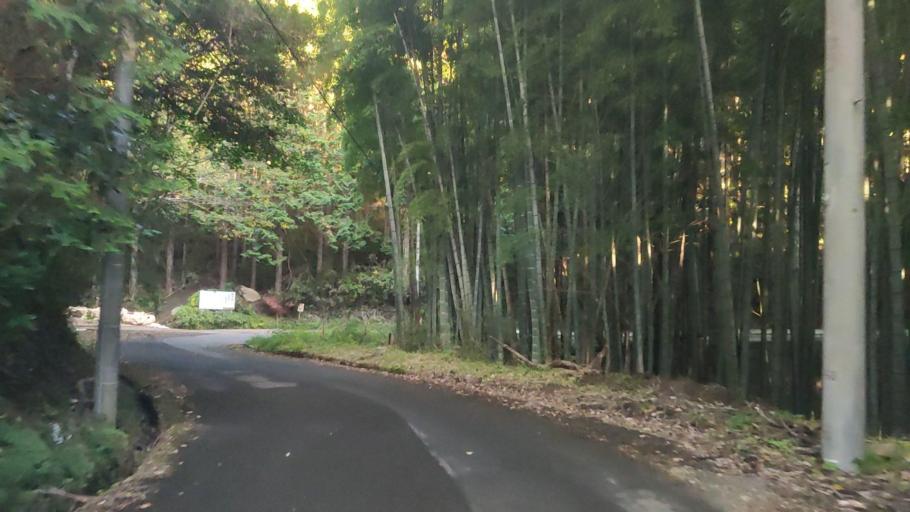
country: JP
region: Kanagawa
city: Hakone
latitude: 35.1331
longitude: 138.9961
